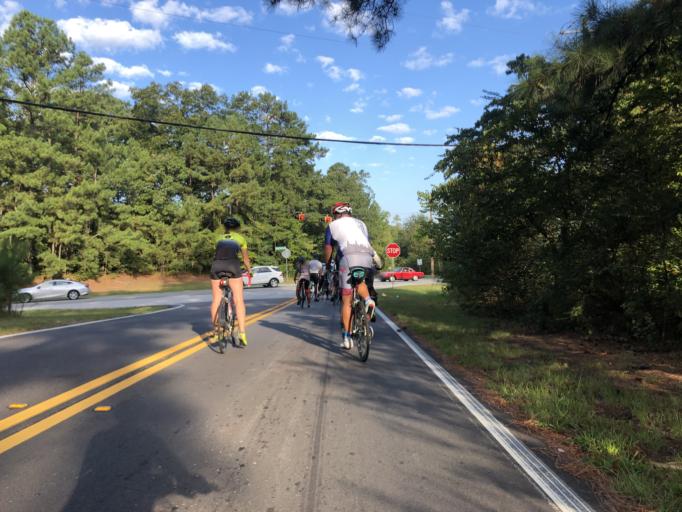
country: US
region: Georgia
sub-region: Fulton County
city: Palmetto
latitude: 33.5732
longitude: -84.6670
